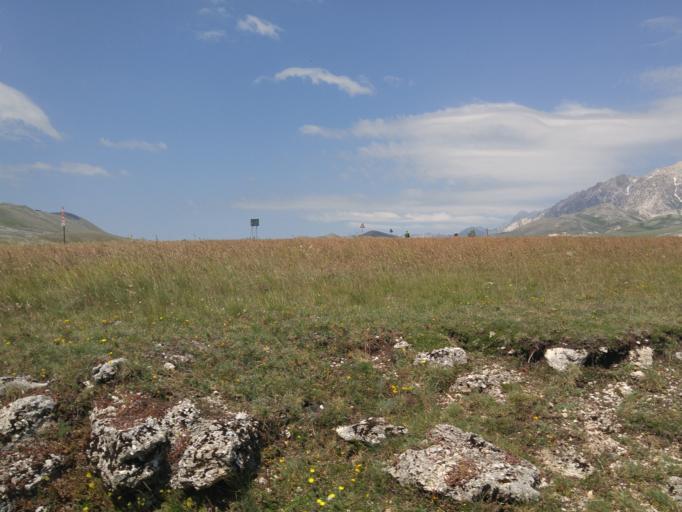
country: IT
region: Abruzzo
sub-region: Provincia dell' Aquila
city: Castel del Monte
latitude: 42.3993
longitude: 13.7554
